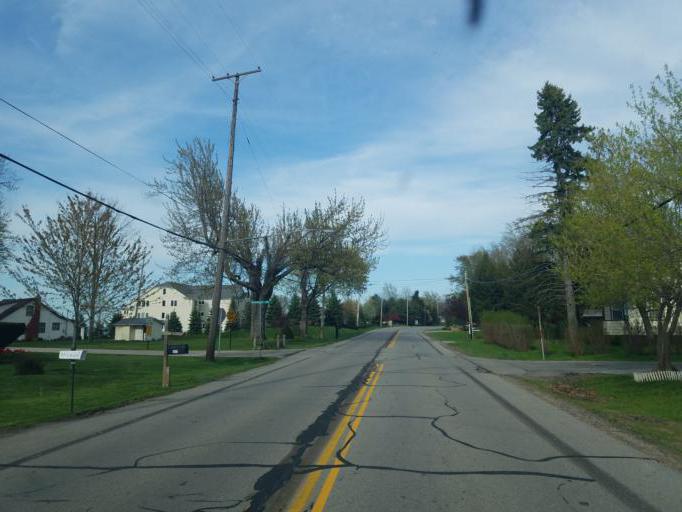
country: US
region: Ohio
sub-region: Ashtabula County
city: Ashtabula
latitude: 41.8795
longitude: -80.8648
